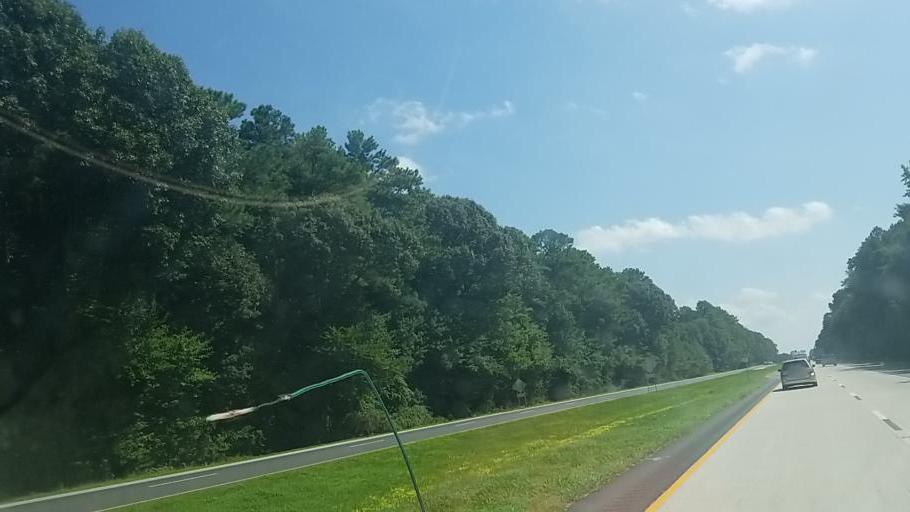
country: US
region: Delaware
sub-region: Sussex County
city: Milford
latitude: 38.8674
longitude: -75.4395
